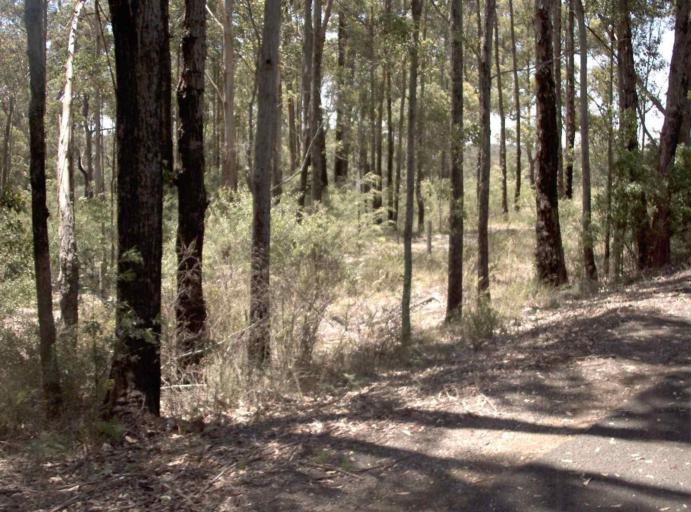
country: AU
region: Victoria
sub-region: East Gippsland
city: Lakes Entrance
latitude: -37.7438
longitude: 148.1657
